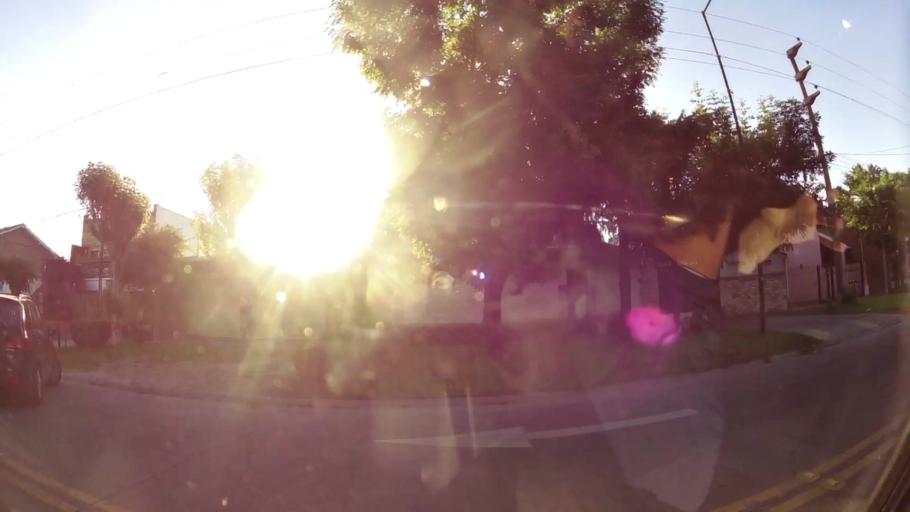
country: AR
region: Buenos Aires
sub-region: Partido de San Isidro
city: San Isidro
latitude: -34.4701
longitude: -58.5553
